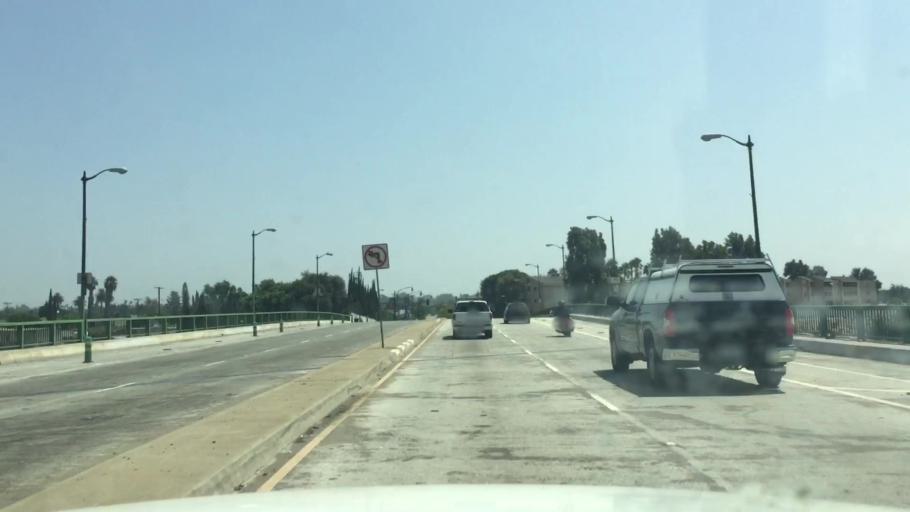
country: US
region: California
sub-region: Los Angeles County
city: East Rancho Dominguez
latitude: 33.8594
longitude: -118.1984
